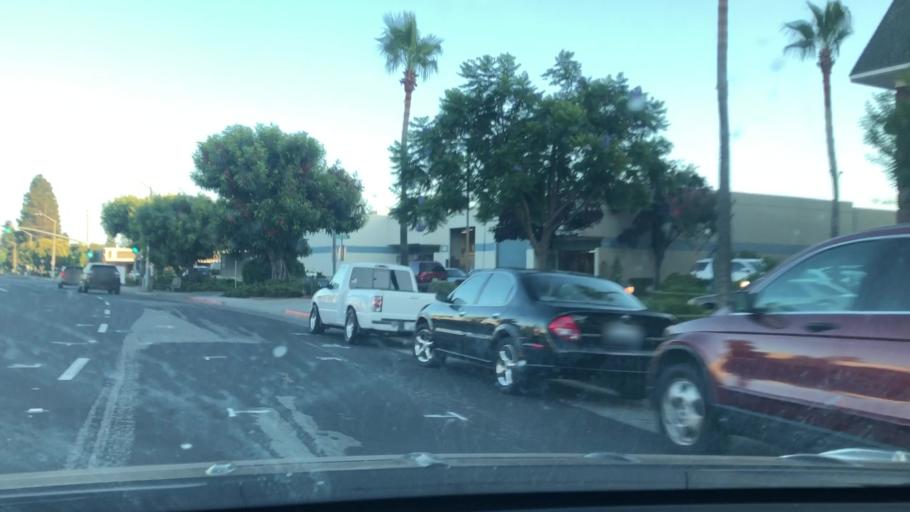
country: US
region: California
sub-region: Santa Clara County
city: Santa Clara
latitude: 37.3868
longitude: -121.9442
